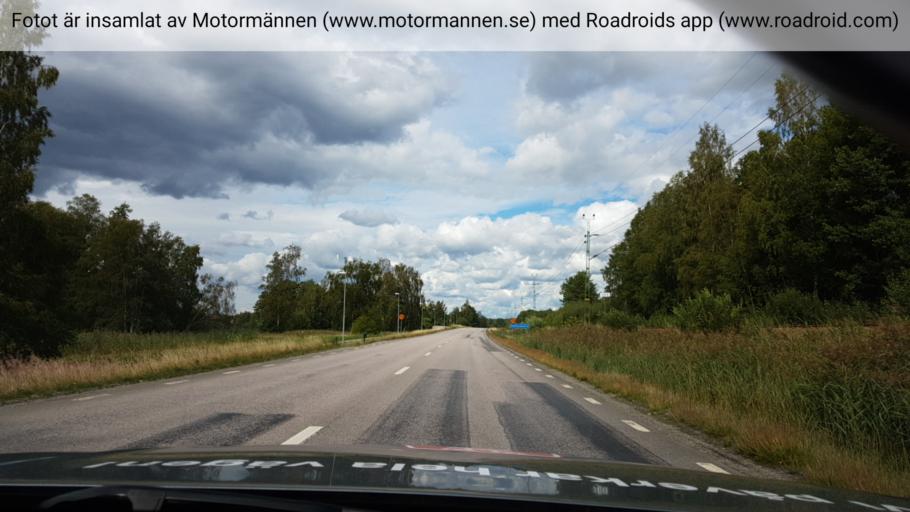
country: SE
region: Uppsala
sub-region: Heby Kommun
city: Morgongava
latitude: 59.9248
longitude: 16.9842
